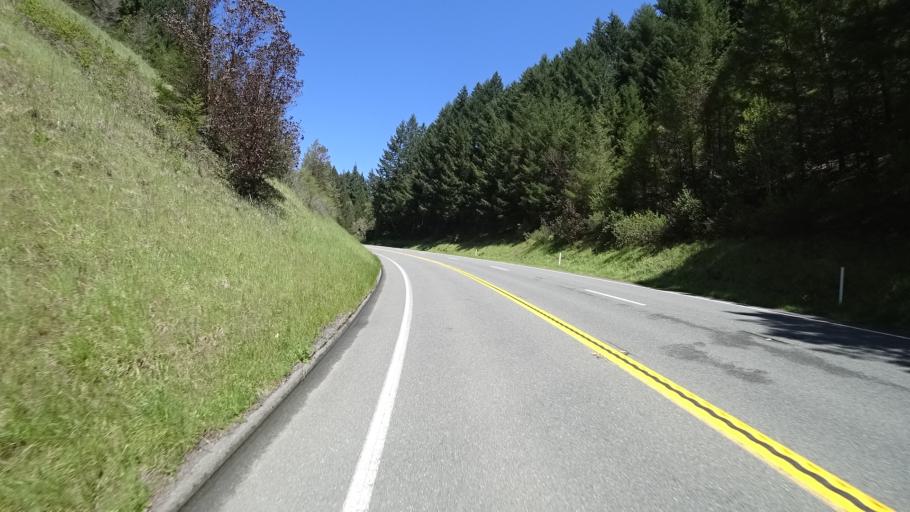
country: US
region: California
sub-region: Humboldt County
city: Blue Lake
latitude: 40.9099
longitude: -123.8243
